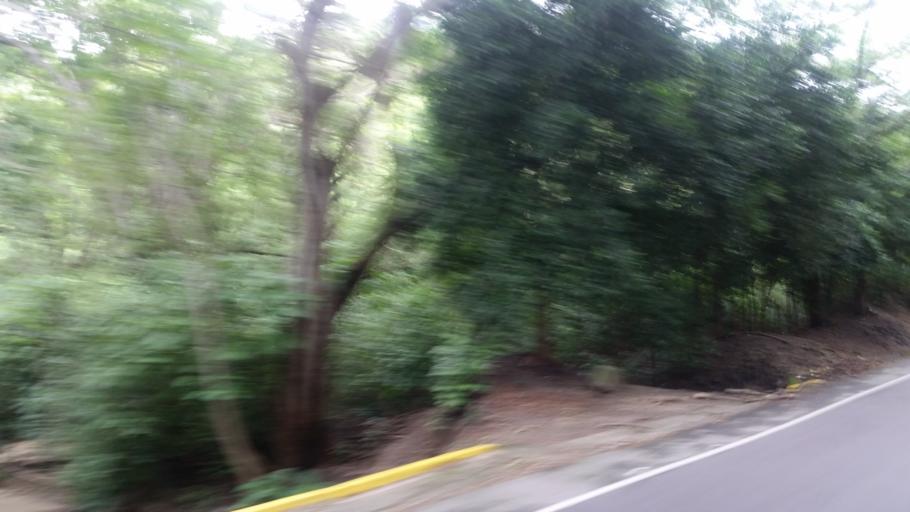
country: CO
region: Magdalena
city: Santa Marta
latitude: 11.2850
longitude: -73.9904
